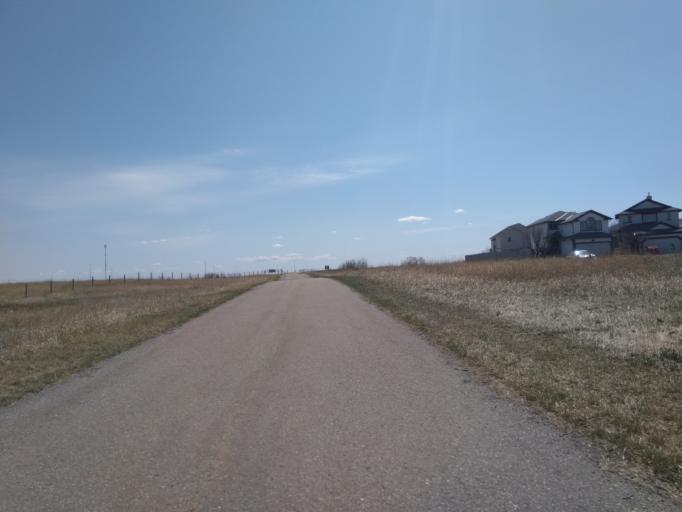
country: CA
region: Alberta
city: Chestermere
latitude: 51.0929
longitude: -113.9259
